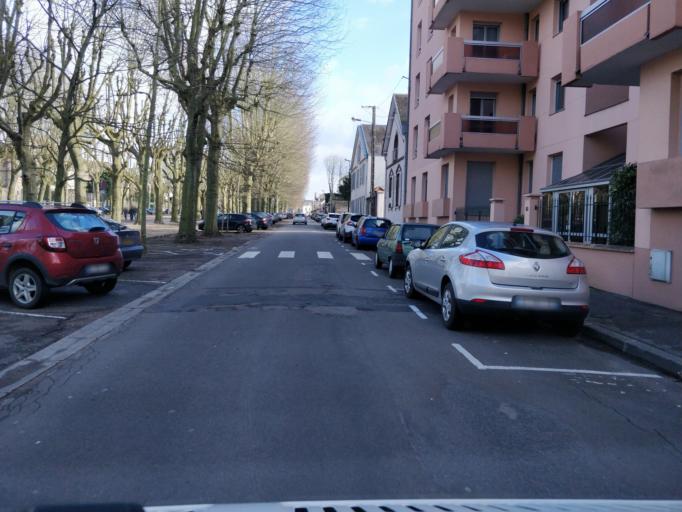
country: FR
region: Bourgogne
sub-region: Departement de l'Yonne
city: Sens
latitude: 48.1950
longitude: 3.2776
